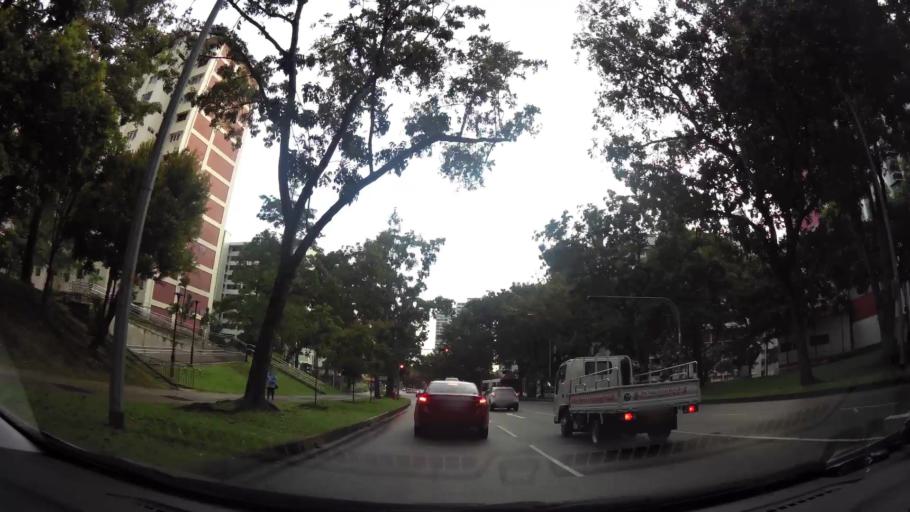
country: SG
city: Singapore
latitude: 1.3645
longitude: 103.8559
